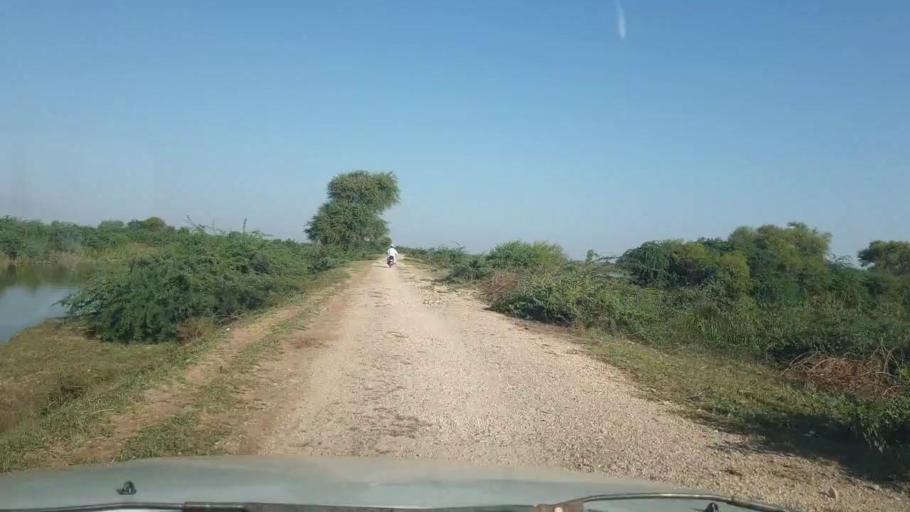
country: PK
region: Sindh
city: Chuhar Jamali
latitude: 24.5451
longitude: 67.9115
